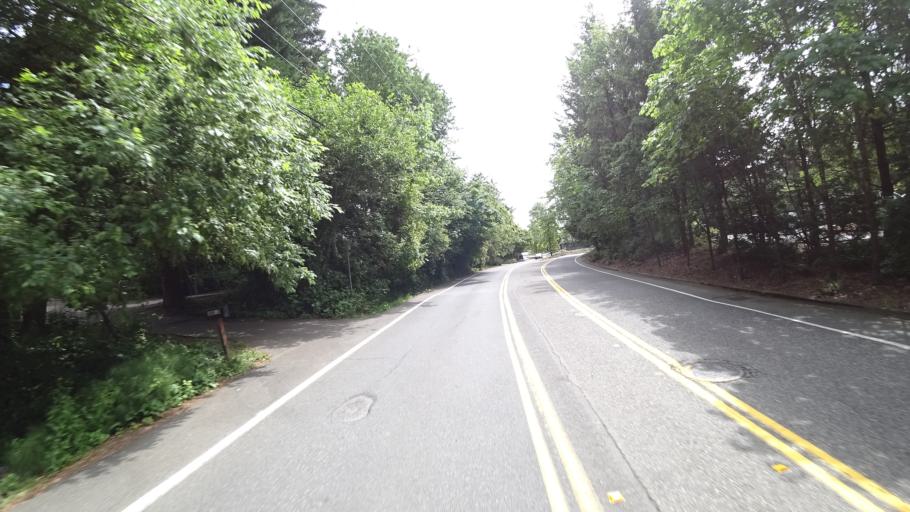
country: US
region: Oregon
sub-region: Clackamas County
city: Lake Oswego
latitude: 45.4532
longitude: -122.6778
